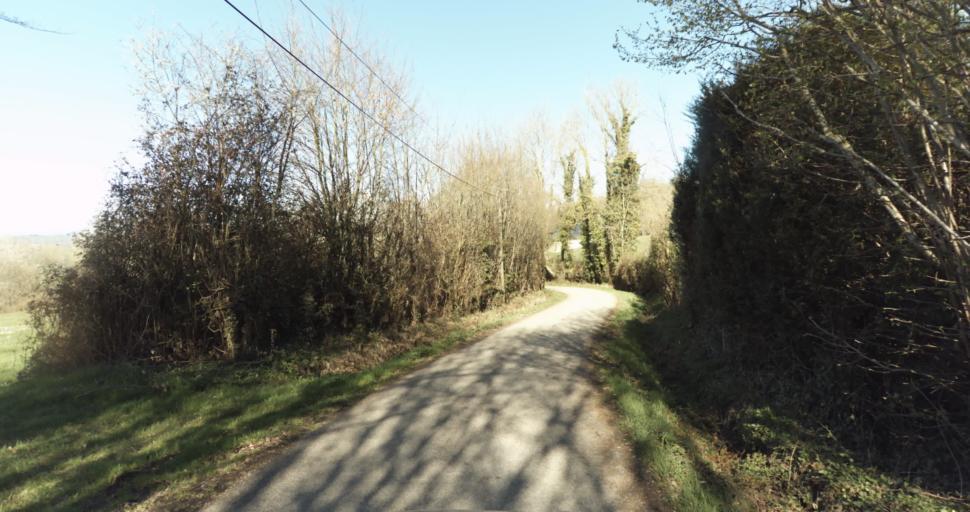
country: FR
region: Lower Normandy
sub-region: Departement du Calvados
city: Livarot
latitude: 48.9538
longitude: 0.0795
